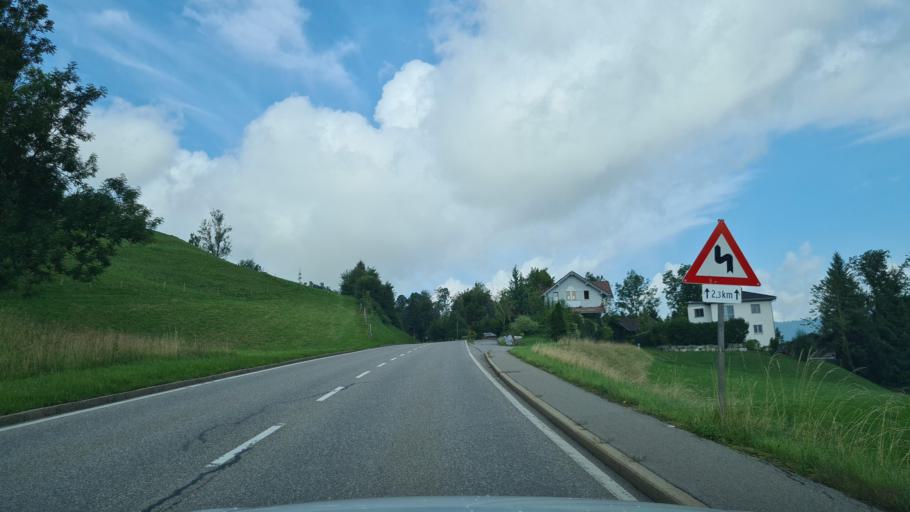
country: AT
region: Vorarlberg
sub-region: Politischer Bezirk Bregenz
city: Egg
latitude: 47.4533
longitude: 9.8760
